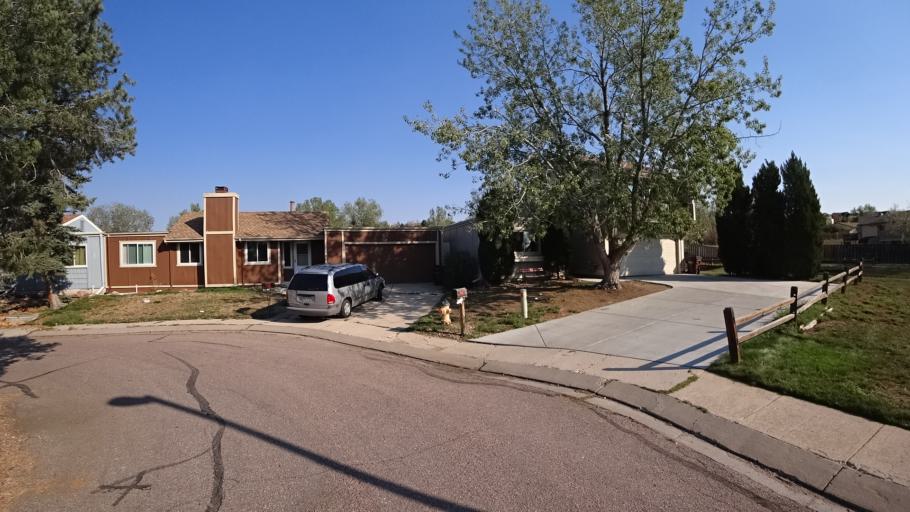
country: US
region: Colorado
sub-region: El Paso County
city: Stratmoor
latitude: 38.7784
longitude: -104.8116
